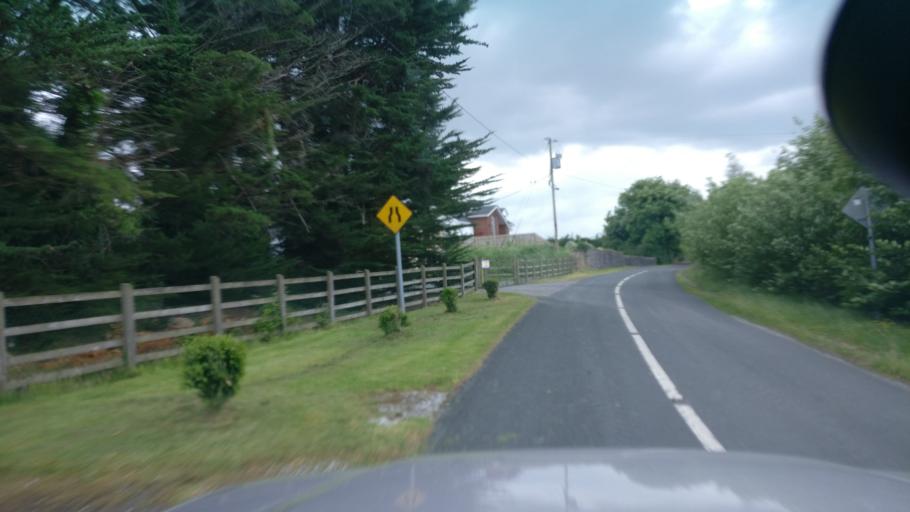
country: IE
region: Connaught
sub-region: County Galway
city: Ballinasloe
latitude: 53.3095
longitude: -8.2684
